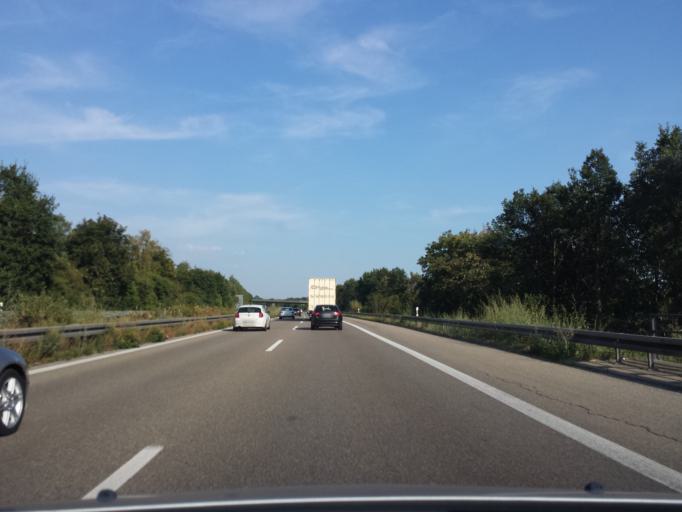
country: DE
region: Bavaria
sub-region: Swabia
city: Senden
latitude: 48.3338
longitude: 10.0430
